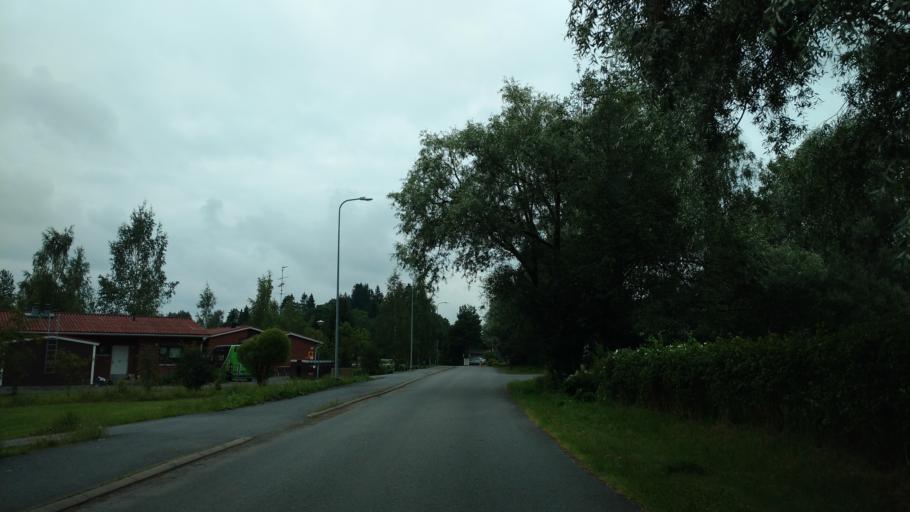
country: FI
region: Haeme
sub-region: Forssa
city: Ypaejae
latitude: 60.8069
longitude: 23.2802
